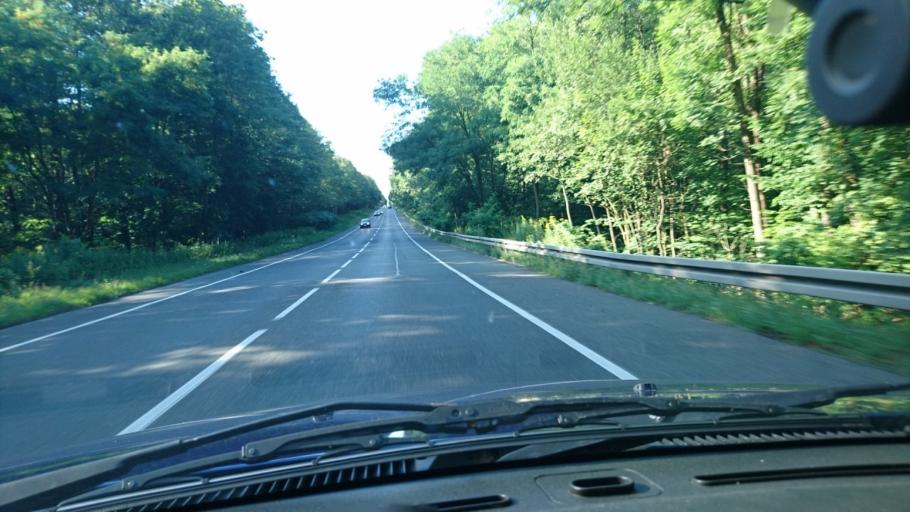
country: PL
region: Silesian Voivodeship
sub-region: Gliwice
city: Gliwice
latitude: 50.3325
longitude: 18.6572
